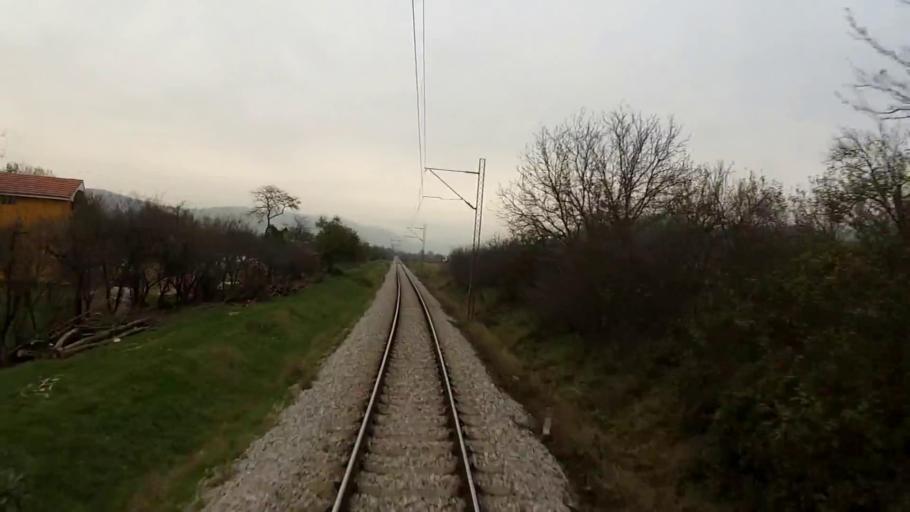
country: RS
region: Central Serbia
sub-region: Pirotski Okrug
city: Dimitrovgrad
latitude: 43.0047
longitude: 22.8099
